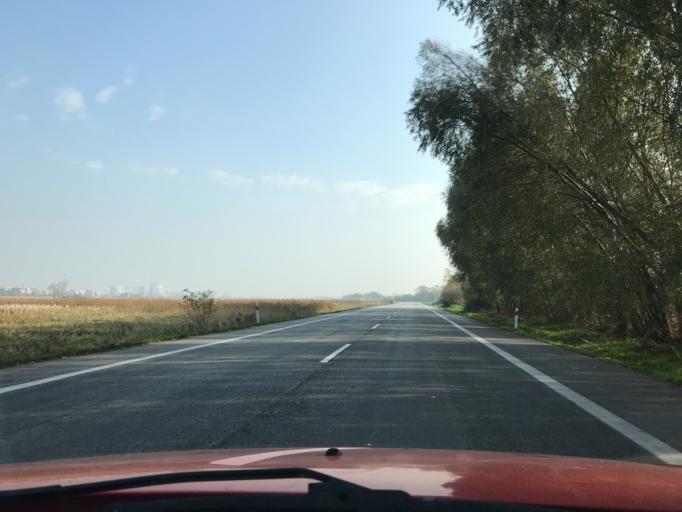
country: PL
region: Greater Poland Voivodeship
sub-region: Powiat sredzki
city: Sroda Wielkopolska
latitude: 52.2243
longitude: 17.2456
